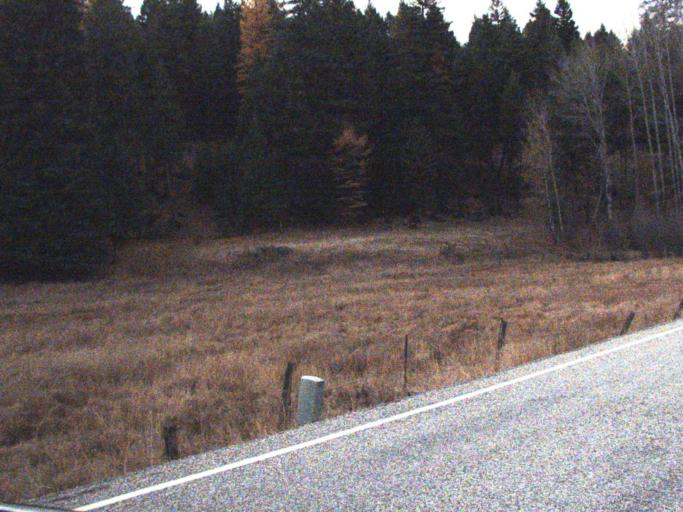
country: US
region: Washington
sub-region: Ferry County
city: Republic
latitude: 48.6072
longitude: -118.6589
